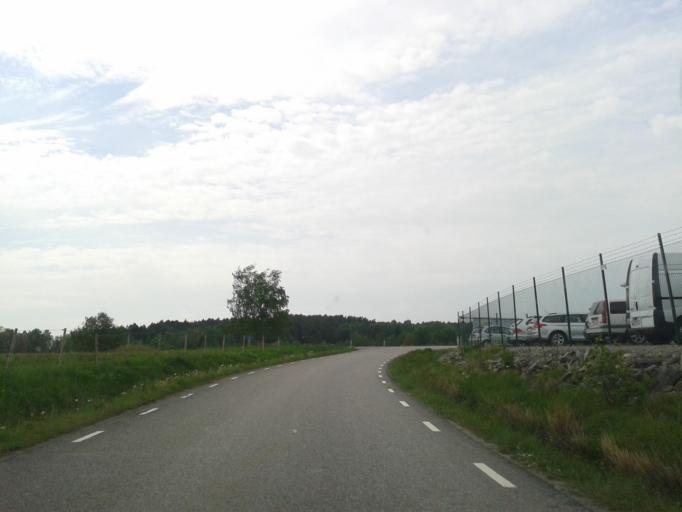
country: SE
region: Vaestra Goetaland
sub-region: Kungalvs Kommun
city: Kungalv
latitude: 57.9198
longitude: 11.9325
